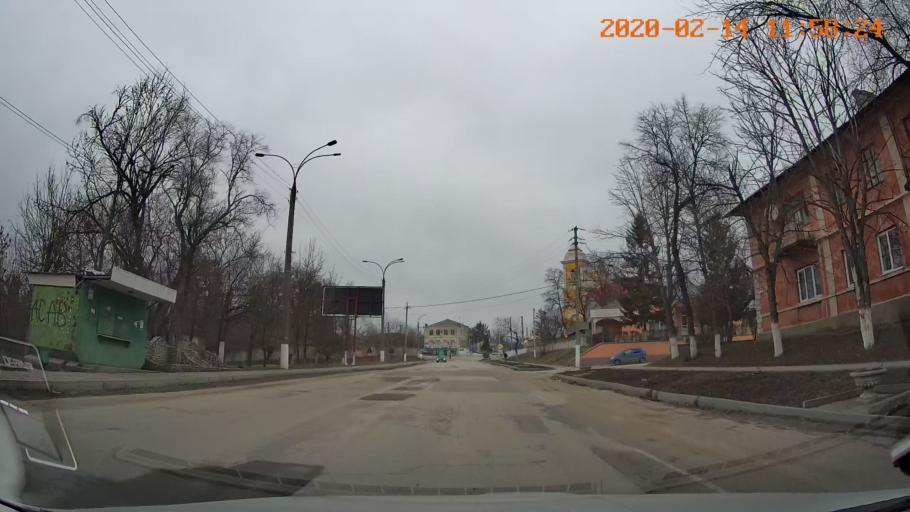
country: RO
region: Botosani
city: Radauti
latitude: 48.2661
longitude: 26.8020
